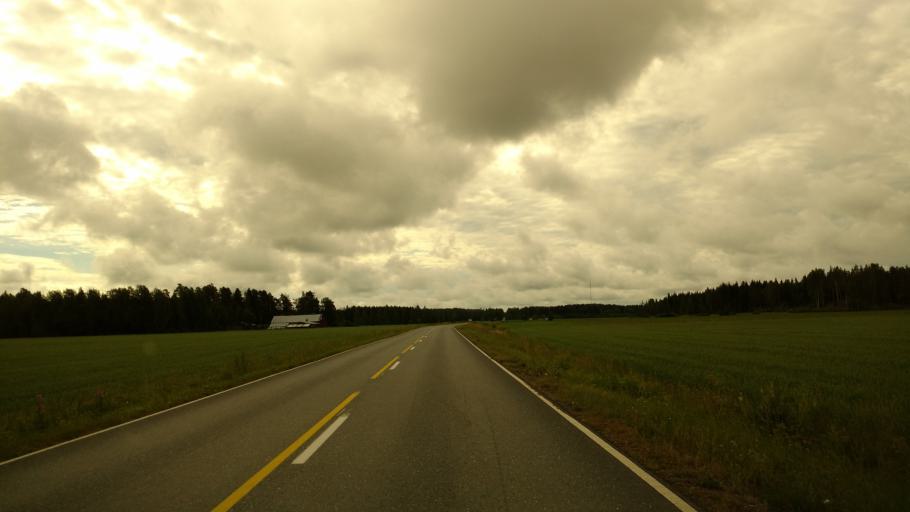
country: FI
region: Varsinais-Suomi
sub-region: Loimaa
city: Koski Tl
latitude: 60.5738
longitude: 23.1402
